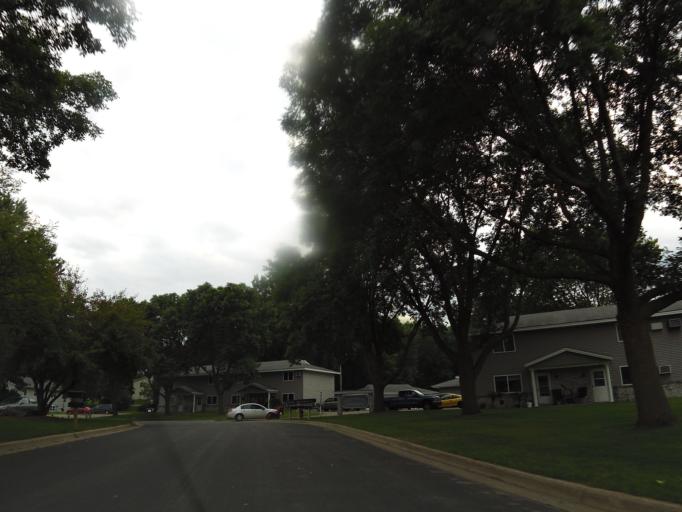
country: US
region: Minnesota
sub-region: Scott County
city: Prior Lake
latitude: 44.7070
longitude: -93.4232
